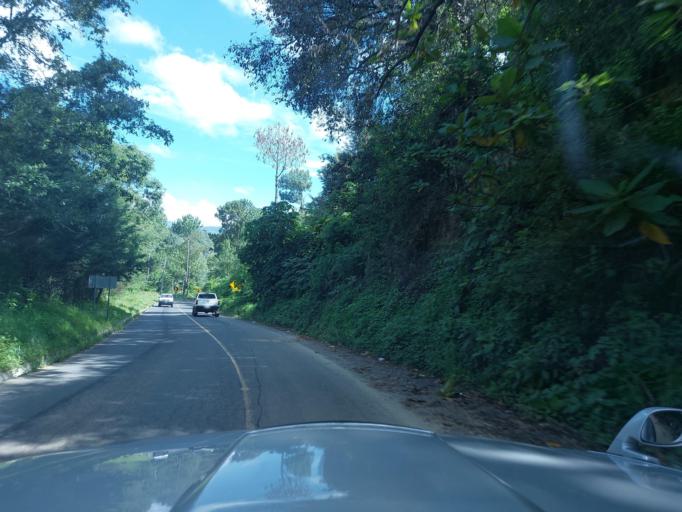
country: GT
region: Chimaltenango
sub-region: Municipio de Santa Cruz Balanya
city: Santa Cruz Balanya
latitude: 14.6813
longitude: -90.8952
